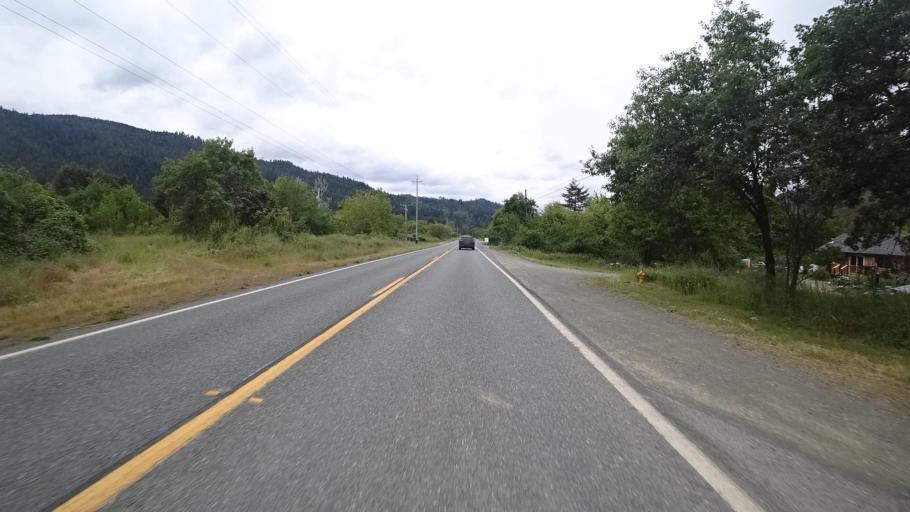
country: US
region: California
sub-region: Humboldt County
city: Willow Creek
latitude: 41.0275
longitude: -123.6577
